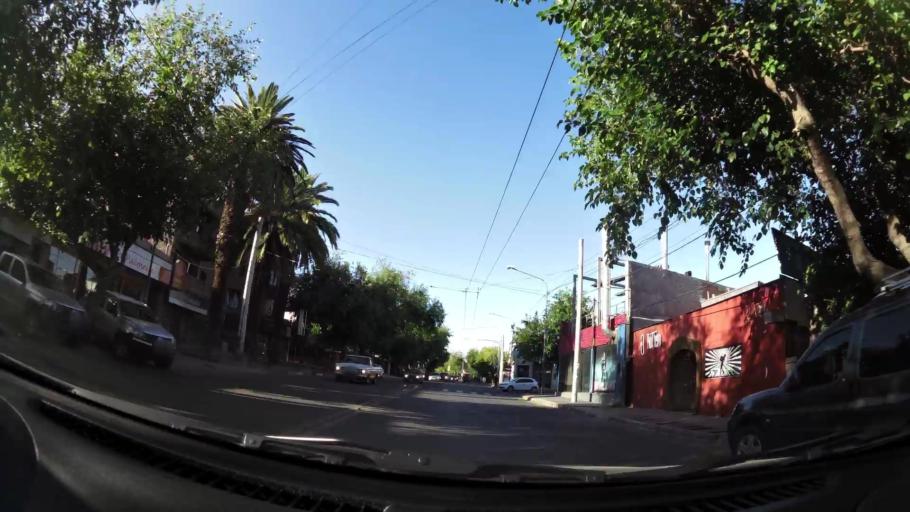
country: AR
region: Mendoza
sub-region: Departamento de Godoy Cruz
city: Godoy Cruz
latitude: -32.9346
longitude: -68.8503
